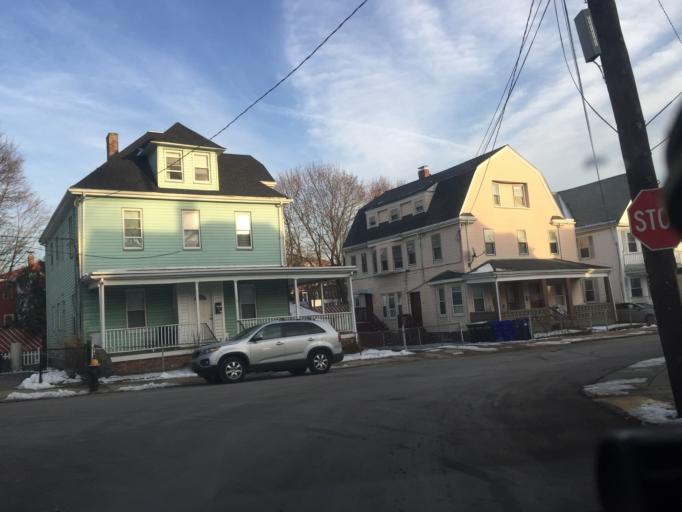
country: US
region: Massachusetts
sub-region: Middlesex County
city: Watertown
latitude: 42.3548
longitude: -71.1586
